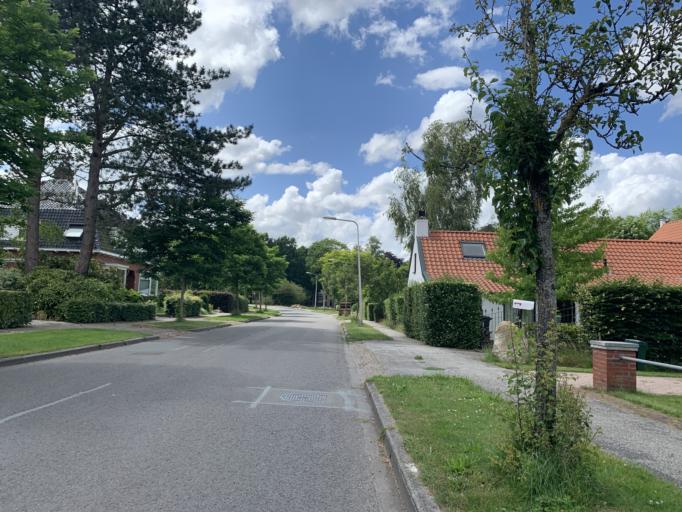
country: NL
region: Groningen
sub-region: Gemeente Haren
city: Haren
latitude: 53.1680
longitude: 6.6161
